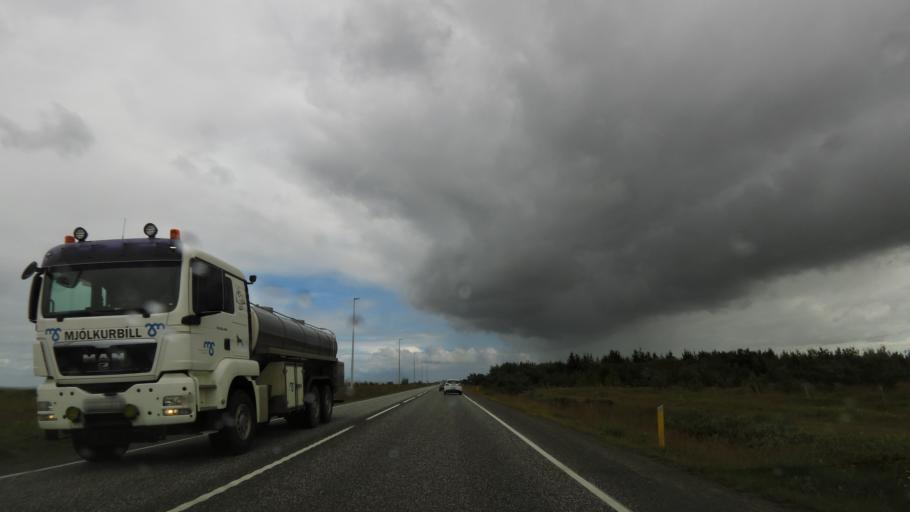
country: IS
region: South
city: Selfoss
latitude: 63.9396
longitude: -20.9652
